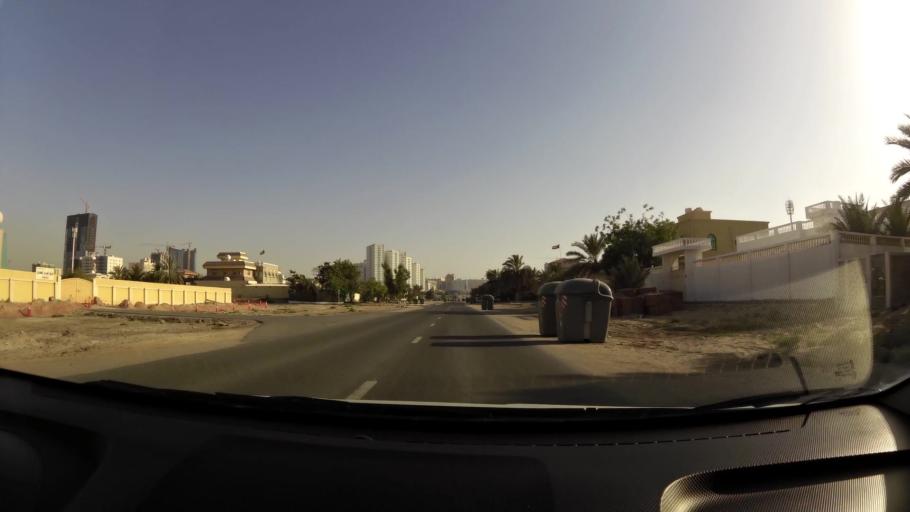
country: AE
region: Ajman
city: Ajman
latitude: 25.4016
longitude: 55.4712
